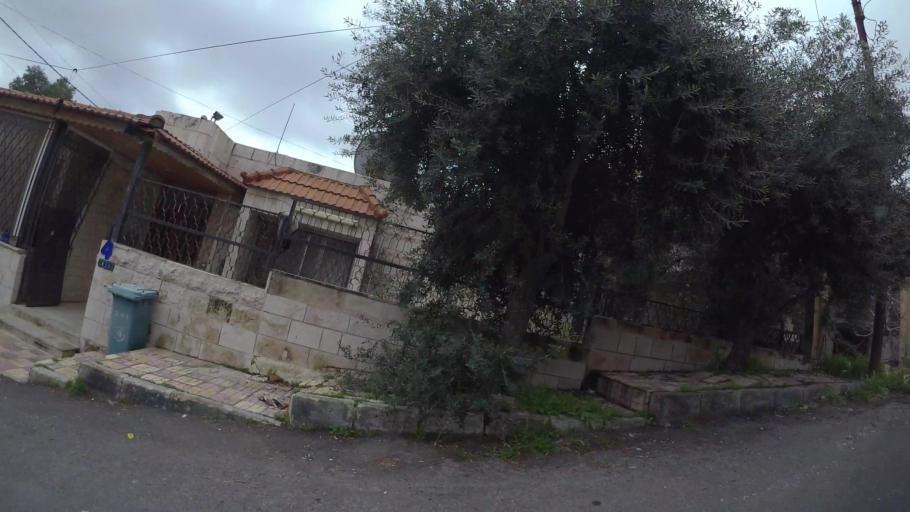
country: JO
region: Amman
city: Wadi as Sir
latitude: 31.9466
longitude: 35.8222
